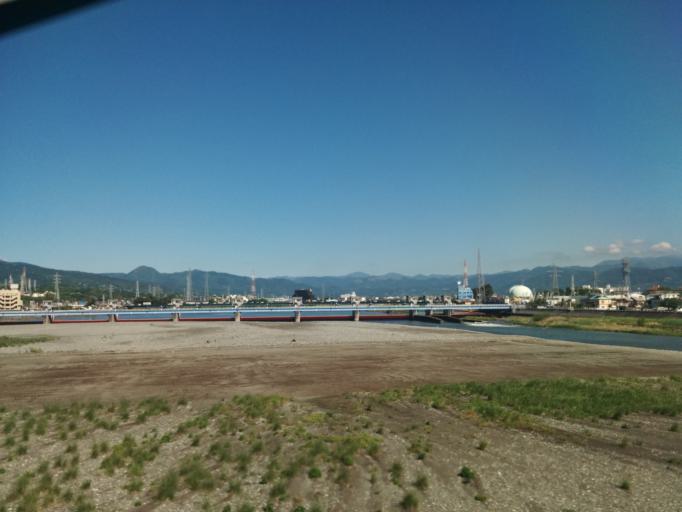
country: JP
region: Kanagawa
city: Odawara
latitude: 35.2705
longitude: 139.1690
